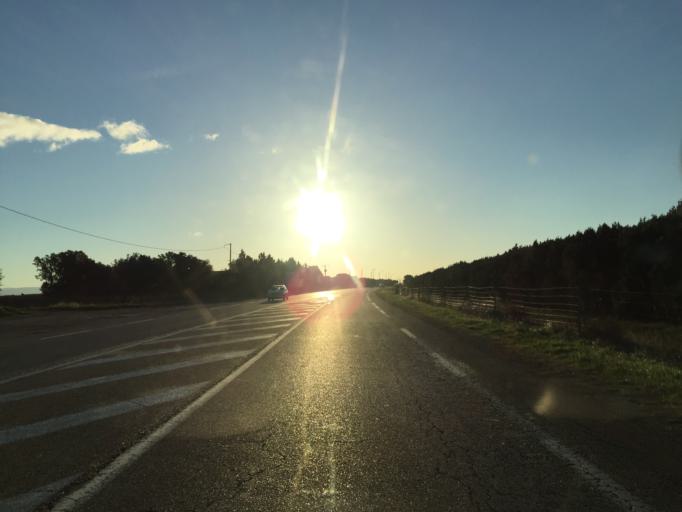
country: FR
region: Provence-Alpes-Cote d'Azur
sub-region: Departement du Vaucluse
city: Courthezon
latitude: 44.0987
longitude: 4.8682
